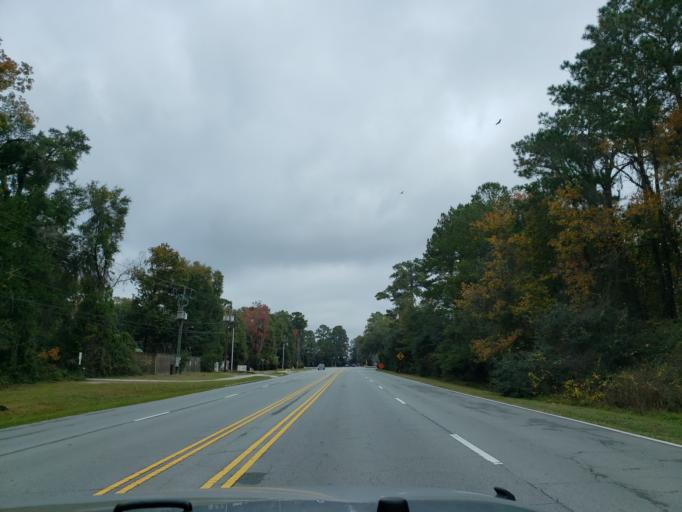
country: US
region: Georgia
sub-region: Chatham County
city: Whitemarsh Island
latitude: 32.0342
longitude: -80.9920
